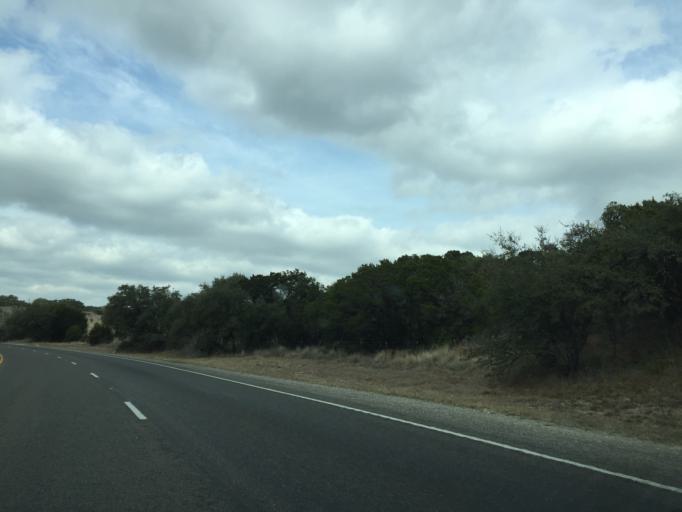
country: US
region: Texas
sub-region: Travis County
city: Briarcliff
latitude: 30.4238
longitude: -98.1294
